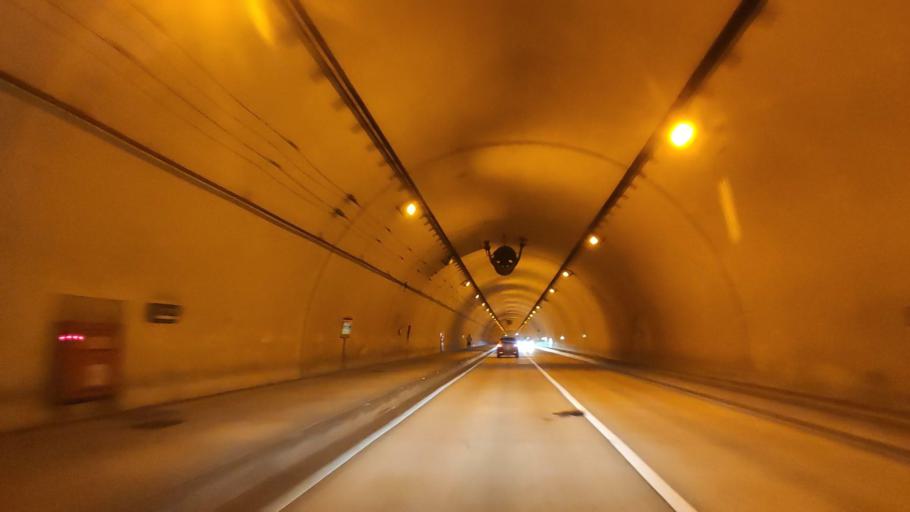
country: JP
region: Ehime
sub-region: Shikoku-chuo Shi
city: Matsuyama
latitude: 33.8777
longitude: 132.7133
